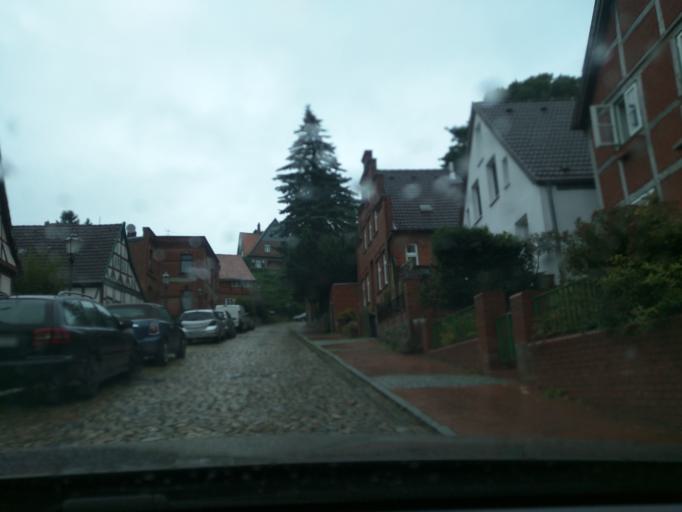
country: DE
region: Schleswig-Holstein
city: Lauenburg
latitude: 53.3711
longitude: 10.5505
